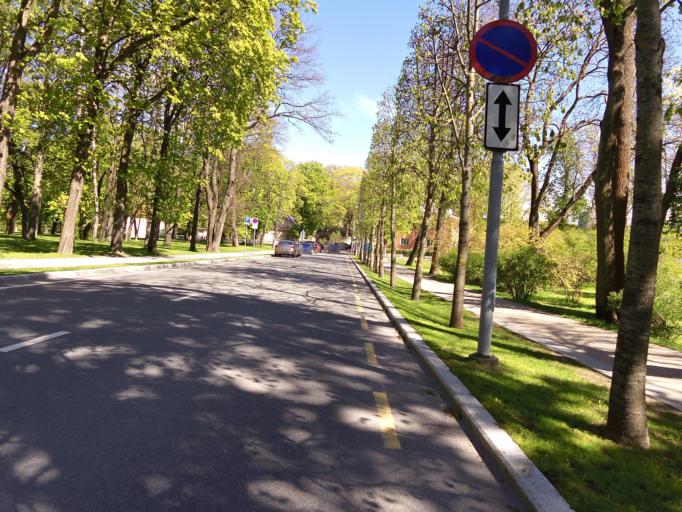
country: EE
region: Harju
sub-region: Tallinna linn
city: Tallinn
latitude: 59.4373
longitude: 24.7941
